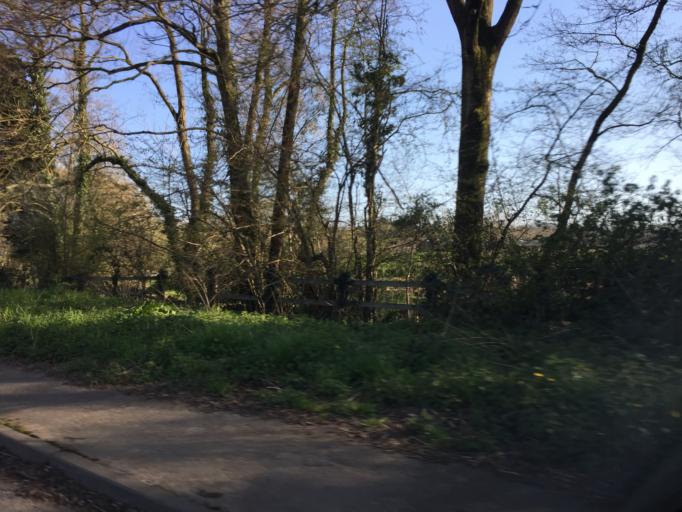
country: GB
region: Wales
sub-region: Monmouthshire
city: Usk
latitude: 51.7168
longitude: -2.9298
